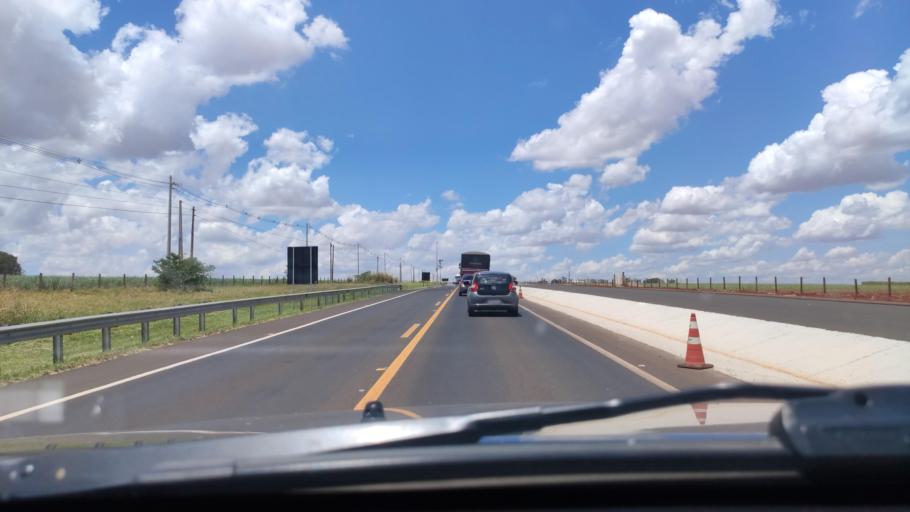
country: BR
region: Sao Paulo
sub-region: Jau
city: Jau
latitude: -22.2455
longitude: -48.5428
